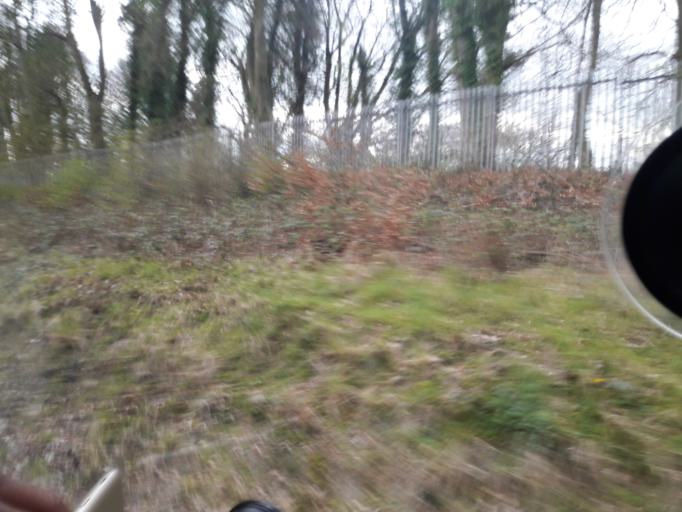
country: IE
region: Leinster
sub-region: An Iarmhi
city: An Muileann gCearr
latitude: 53.5271
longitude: -7.3477
